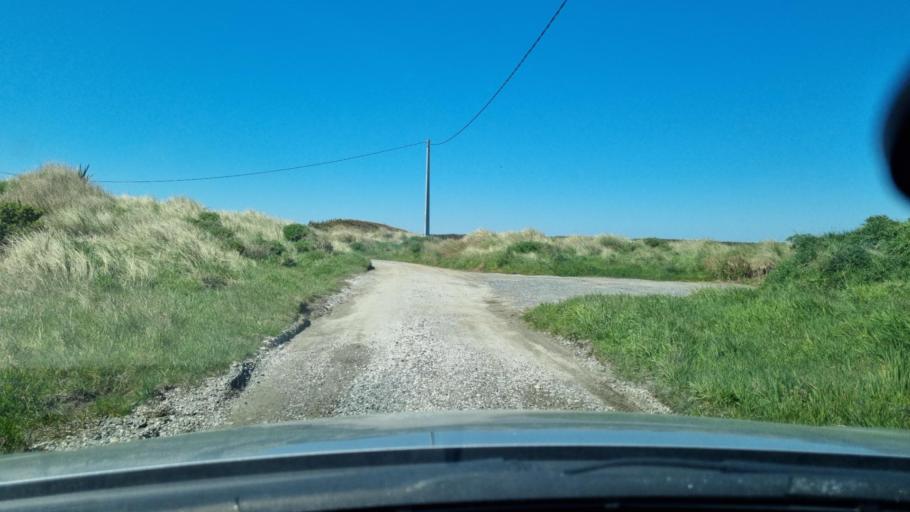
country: NZ
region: Southland
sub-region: Invercargill City
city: Invercargill
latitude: -46.4298
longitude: 168.2288
